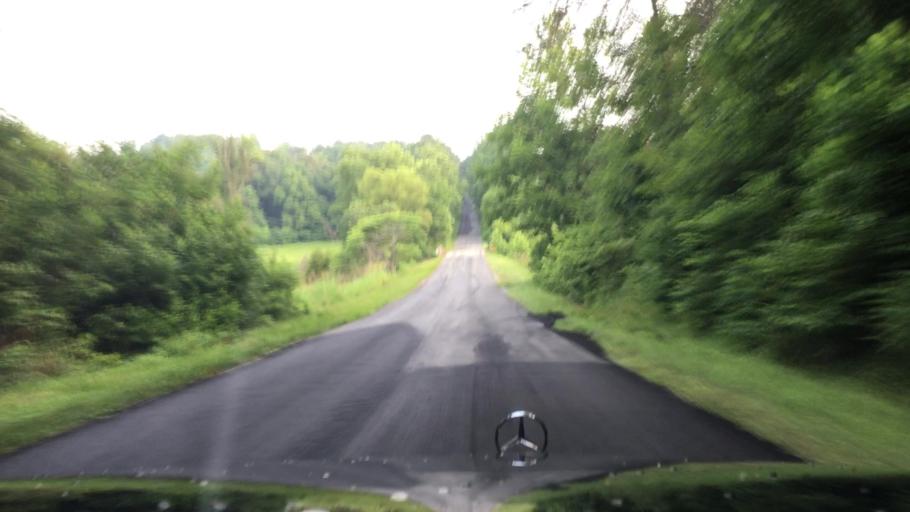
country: US
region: Virginia
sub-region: Campbell County
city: Timberlake
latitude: 37.2465
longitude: -79.3045
